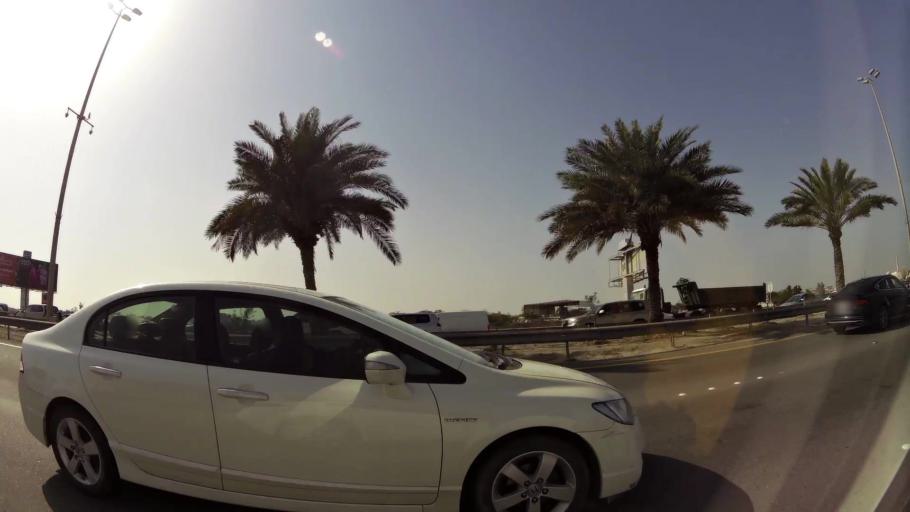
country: BH
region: Manama
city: Jidd Hafs
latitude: 26.2098
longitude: 50.5179
